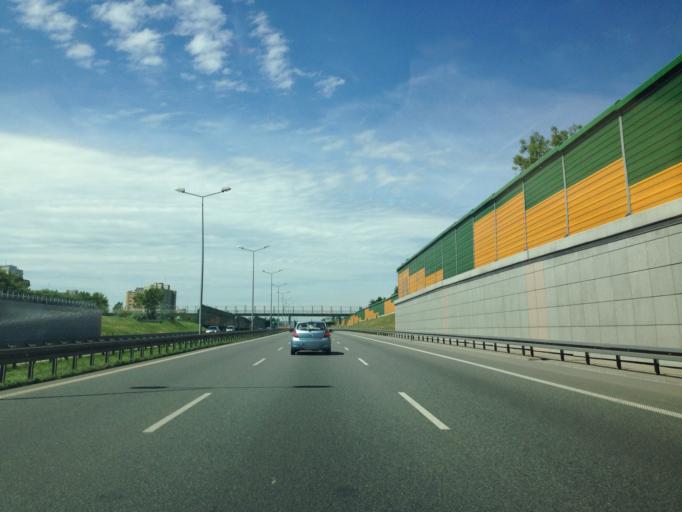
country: PL
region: Masovian Voivodeship
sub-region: Warszawa
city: Bemowo
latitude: 52.2473
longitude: 20.9207
